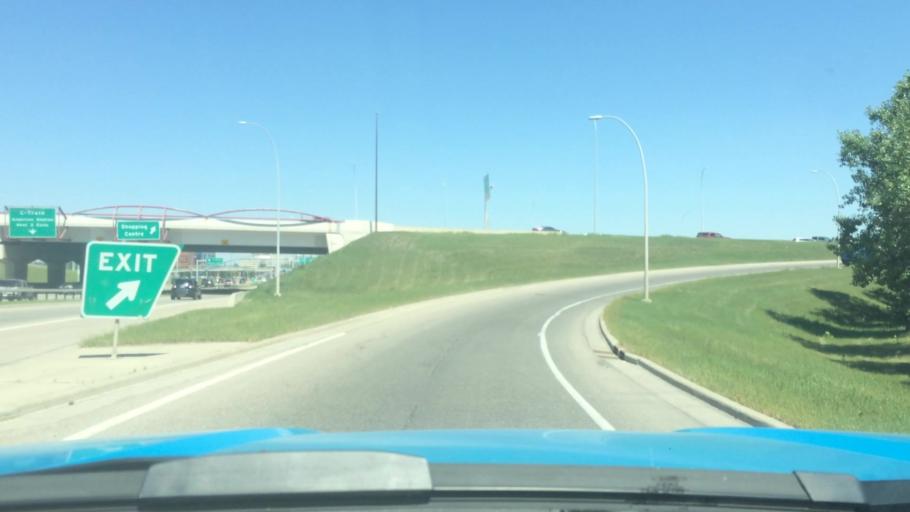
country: CA
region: Alberta
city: Calgary
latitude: 50.9493
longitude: -114.0705
